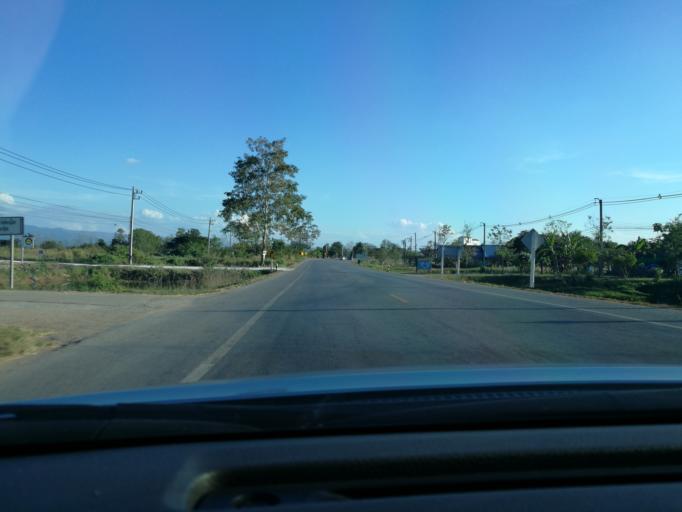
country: TH
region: Phitsanulok
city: Nakhon Thai
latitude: 17.0562
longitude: 100.8103
